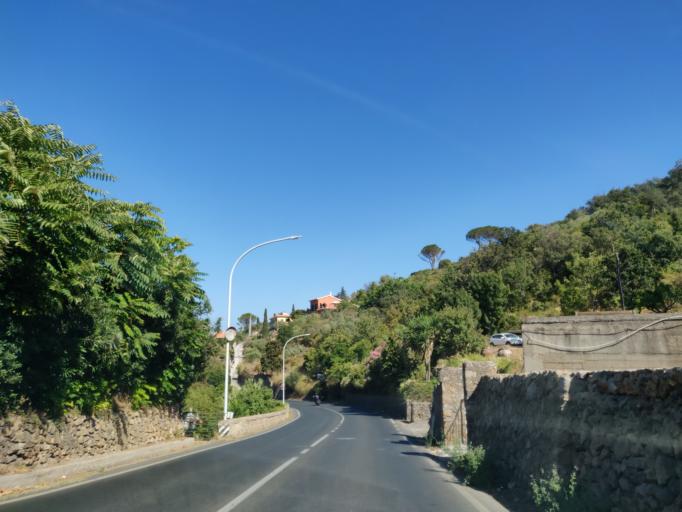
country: IT
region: Tuscany
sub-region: Provincia di Grosseto
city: Monte Argentario
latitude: 42.4367
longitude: 11.1304
